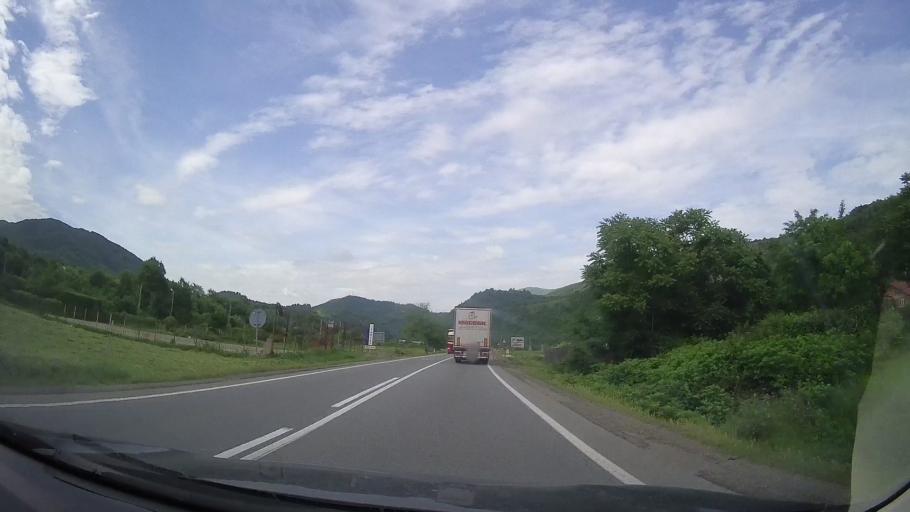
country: RO
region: Caras-Severin
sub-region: Comuna Toplet
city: Toplet
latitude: 44.8136
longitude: 22.3859
